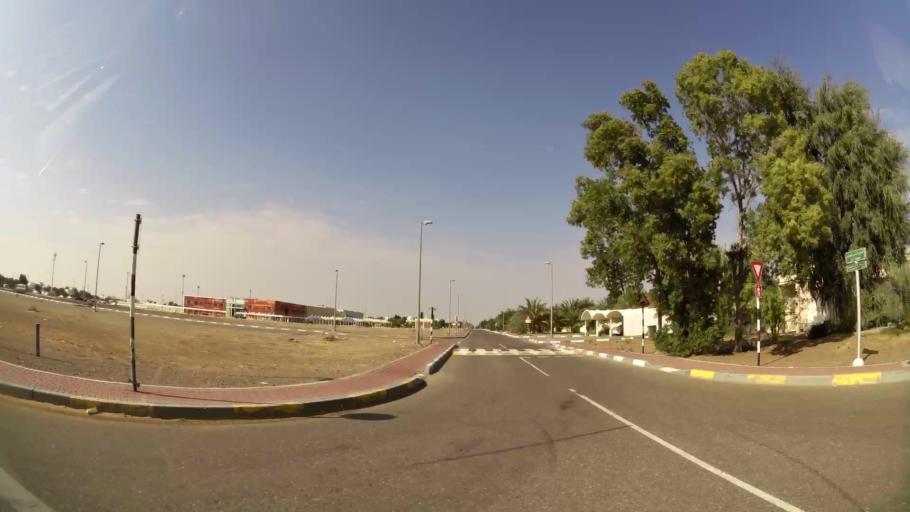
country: AE
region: Abu Dhabi
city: Al Ain
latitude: 24.0699
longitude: 55.8686
